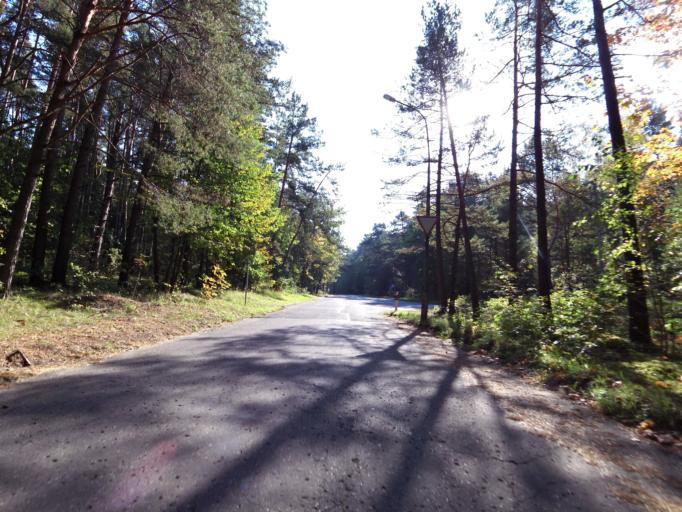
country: LT
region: Vilnius County
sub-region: Vilnius
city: Vilnius
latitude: 54.7314
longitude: 25.3079
